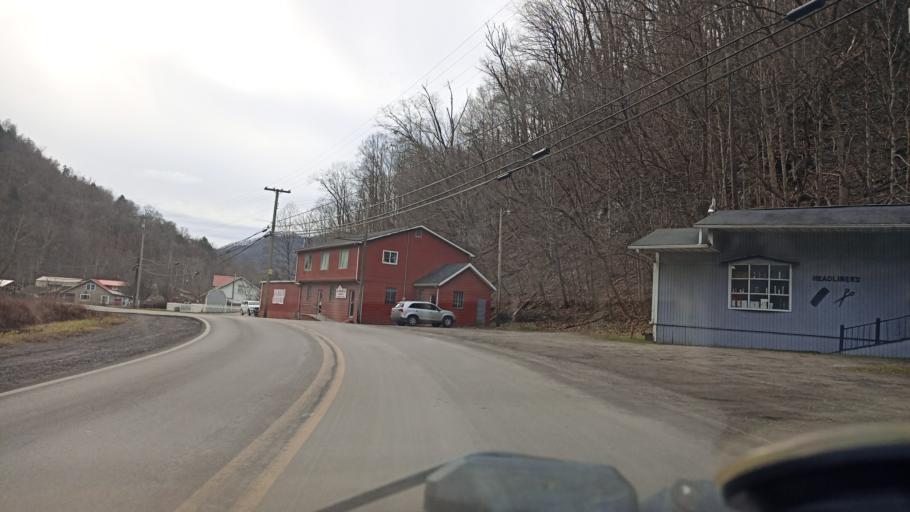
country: US
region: West Virginia
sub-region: Logan County
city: Mallory
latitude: 37.7563
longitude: -81.8600
